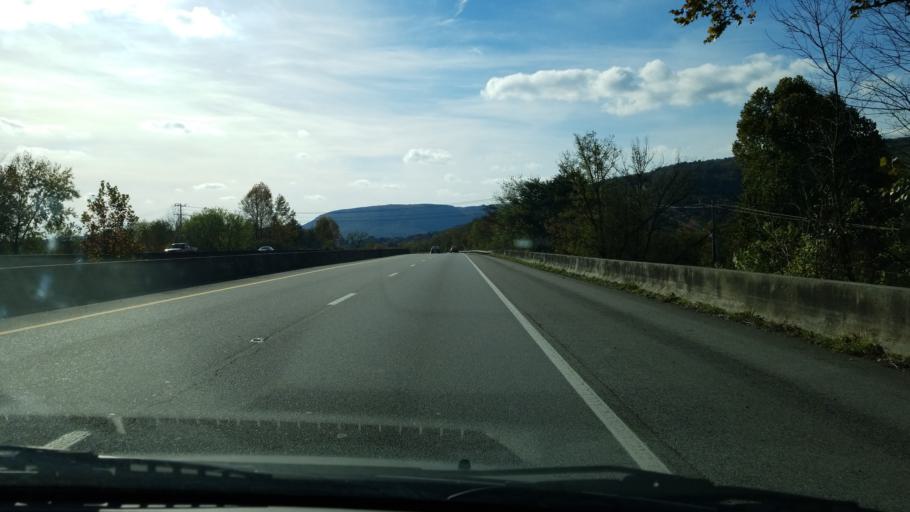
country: US
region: Tennessee
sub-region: Hamilton County
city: Soddy-Daisy
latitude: 35.2395
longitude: -85.1876
